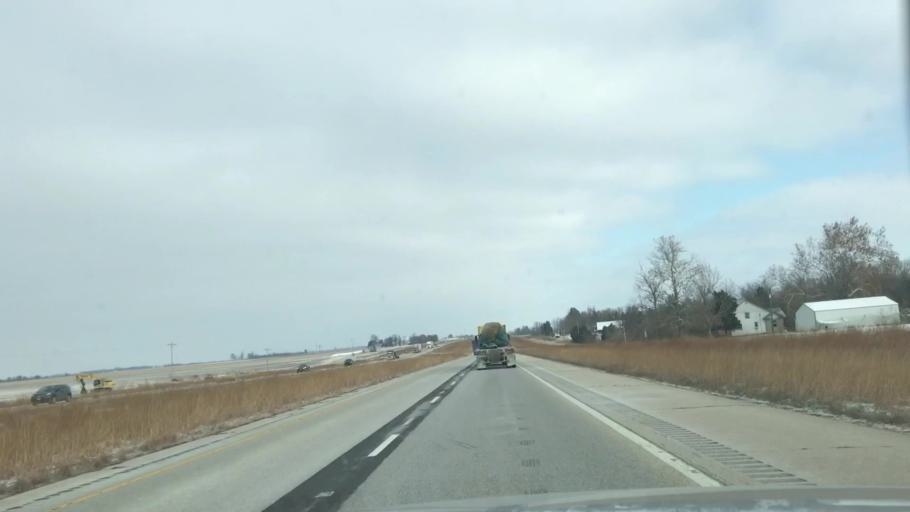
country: US
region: Illinois
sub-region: Sangamon County
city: Divernon
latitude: 39.5038
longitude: -89.6451
